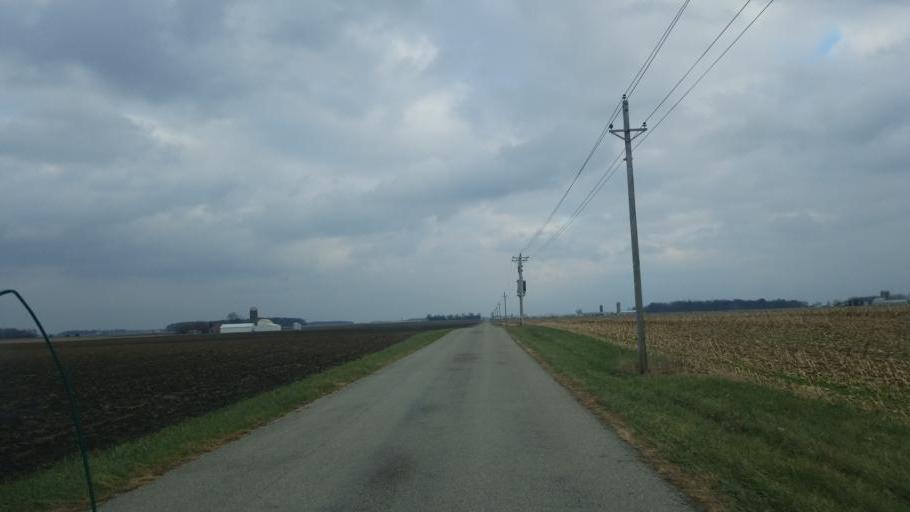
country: US
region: Indiana
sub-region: Adams County
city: Geneva
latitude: 40.5135
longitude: -84.8567
